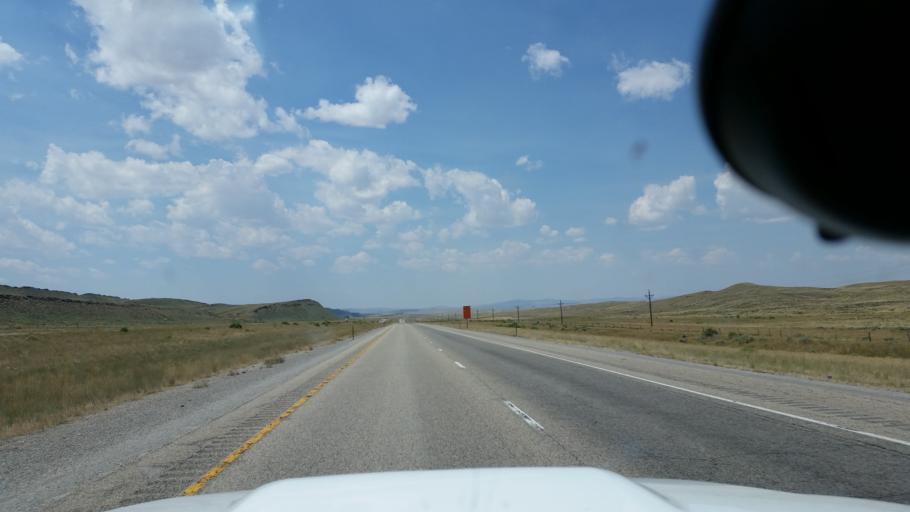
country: US
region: Wyoming
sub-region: Carbon County
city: Saratoga
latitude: 41.7433
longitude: -106.8772
